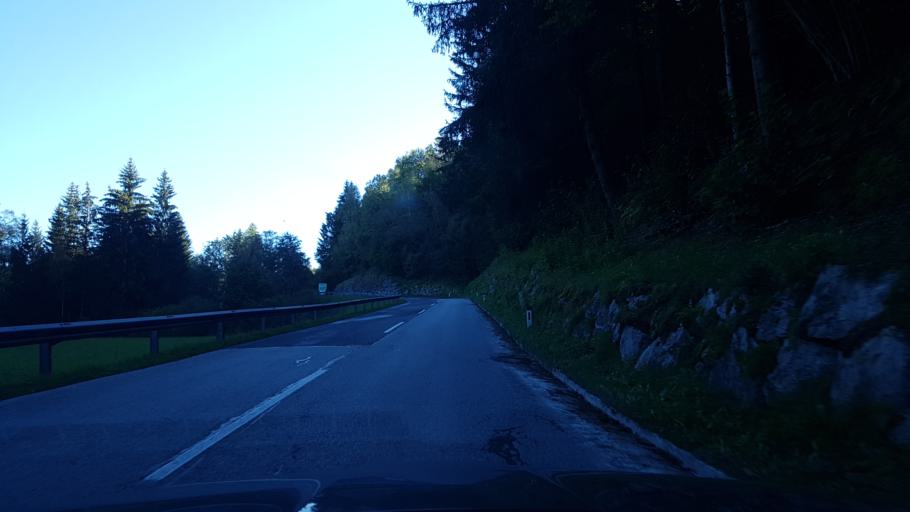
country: AT
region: Styria
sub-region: Politischer Bezirk Liezen
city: Grosssolk
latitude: 47.4348
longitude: 13.9445
